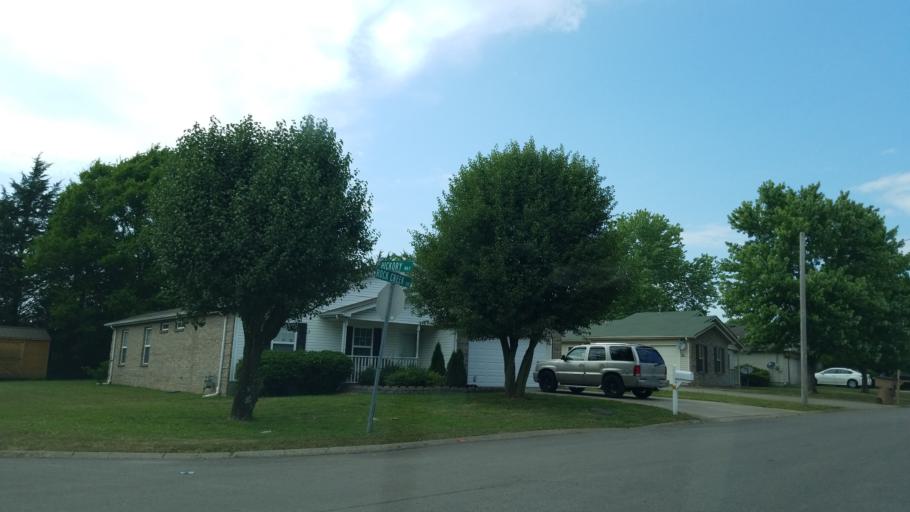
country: US
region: Tennessee
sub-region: Rutherford County
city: La Vergne
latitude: 36.0313
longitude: -86.5901
